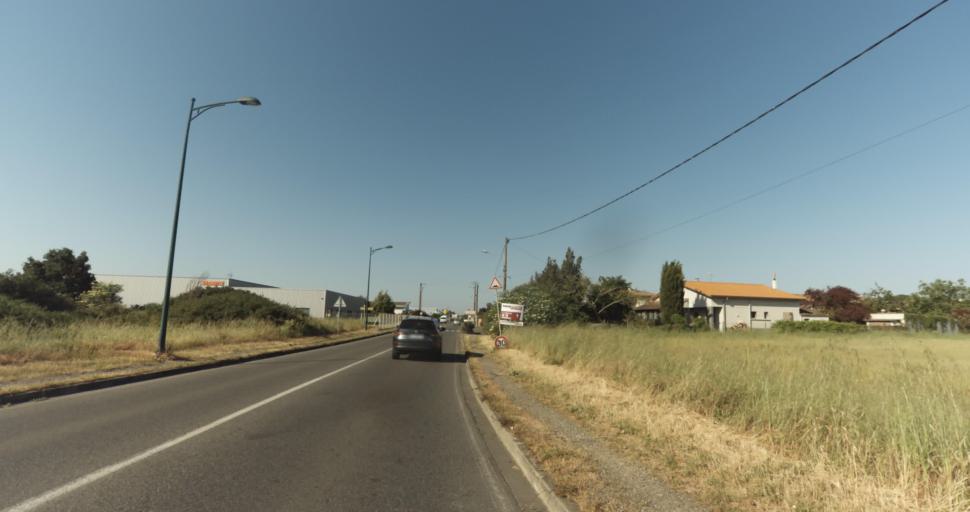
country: FR
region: Midi-Pyrenees
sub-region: Departement de la Haute-Garonne
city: Fonsorbes
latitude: 43.5510
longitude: 1.2442
